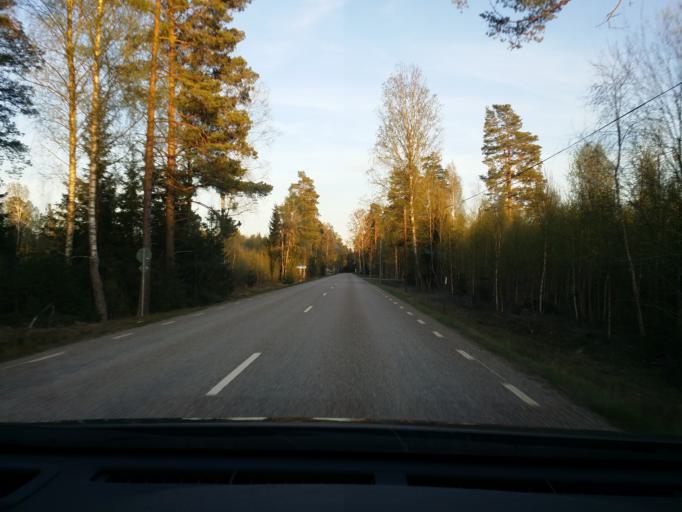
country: SE
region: Vaestmanland
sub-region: Sala Kommun
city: Sala
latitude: 59.8283
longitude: 16.5173
